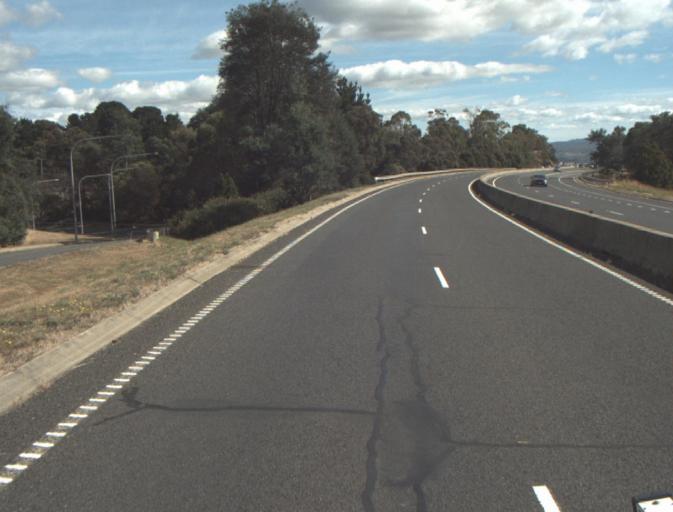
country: AU
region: Tasmania
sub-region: Launceston
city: Summerhill
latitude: -41.4737
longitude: 147.1429
